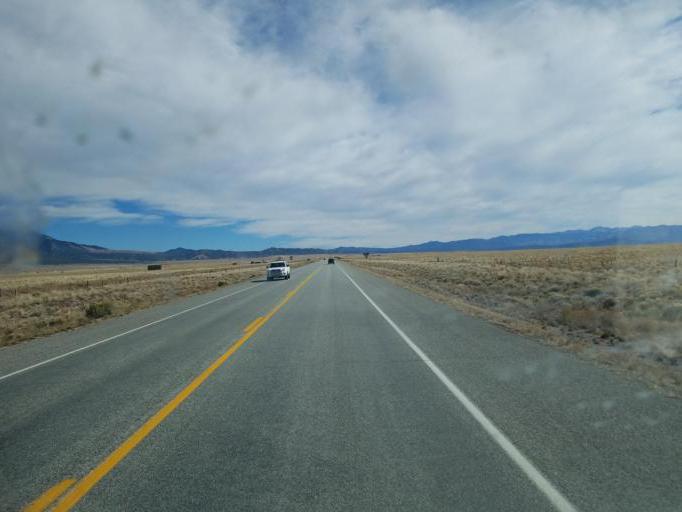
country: US
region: Colorado
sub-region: Alamosa County
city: Alamosa East
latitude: 37.4750
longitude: -105.6124
